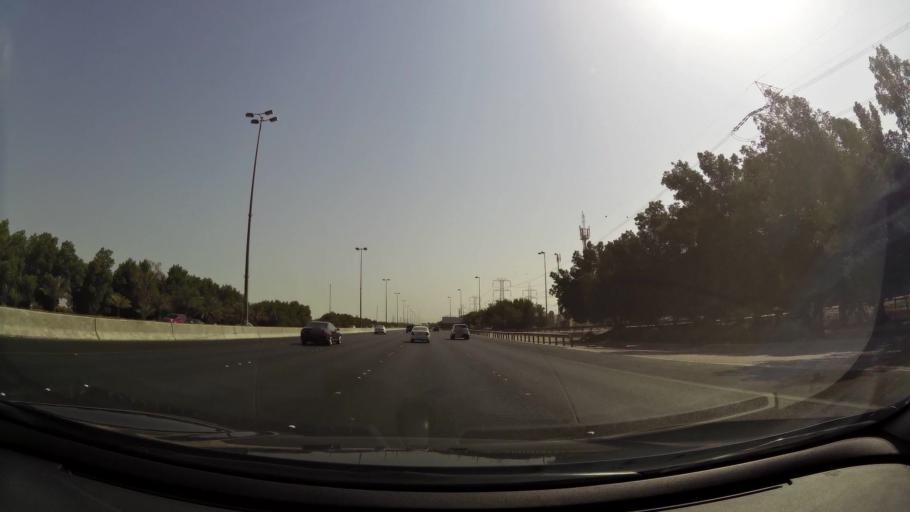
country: KW
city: Bayan
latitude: 29.2898
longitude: 48.0297
